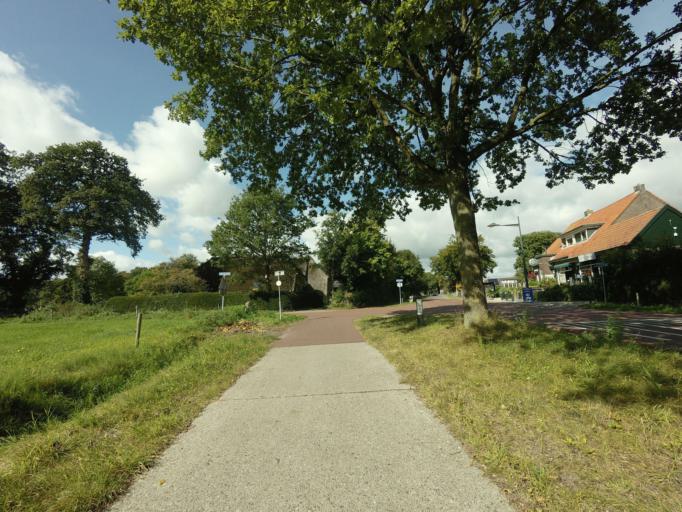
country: NL
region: Overijssel
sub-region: Gemeente Olst-Wijhe
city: Boskamp
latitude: 52.3261
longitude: 6.1303
